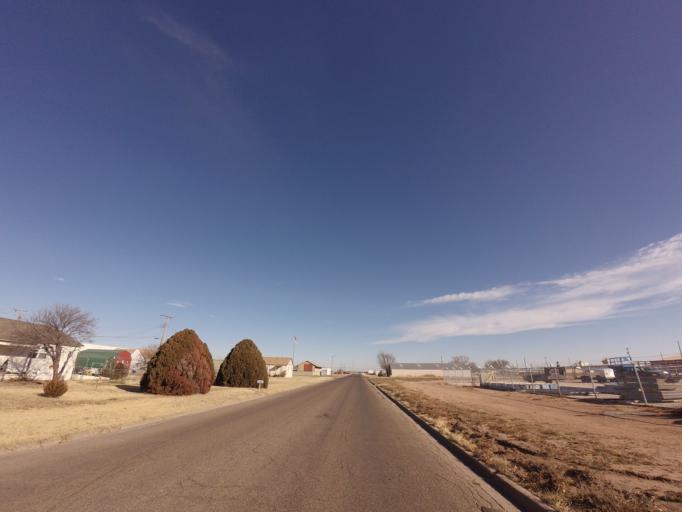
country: US
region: New Mexico
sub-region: Curry County
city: Clovis
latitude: 34.4007
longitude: -103.1825
